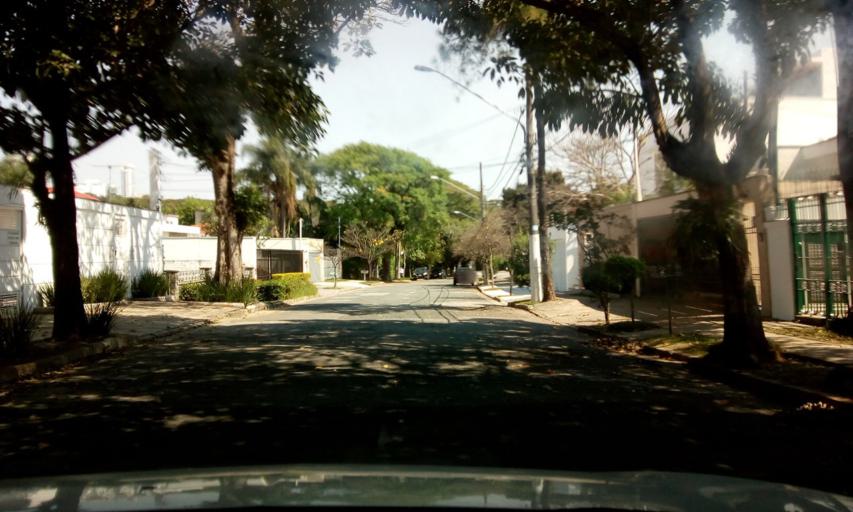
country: BR
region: Sao Paulo
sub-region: Osasco
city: Osasco
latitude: -23.5218
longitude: -46.7136
